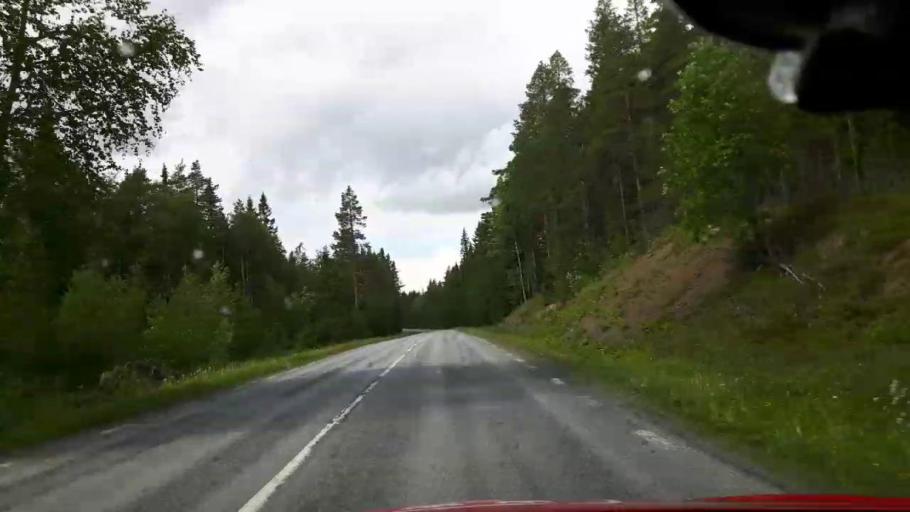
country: SE
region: Jaemtland
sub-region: Krokoms Kommun
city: Krokom
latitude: 63.4052
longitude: 14.2723
